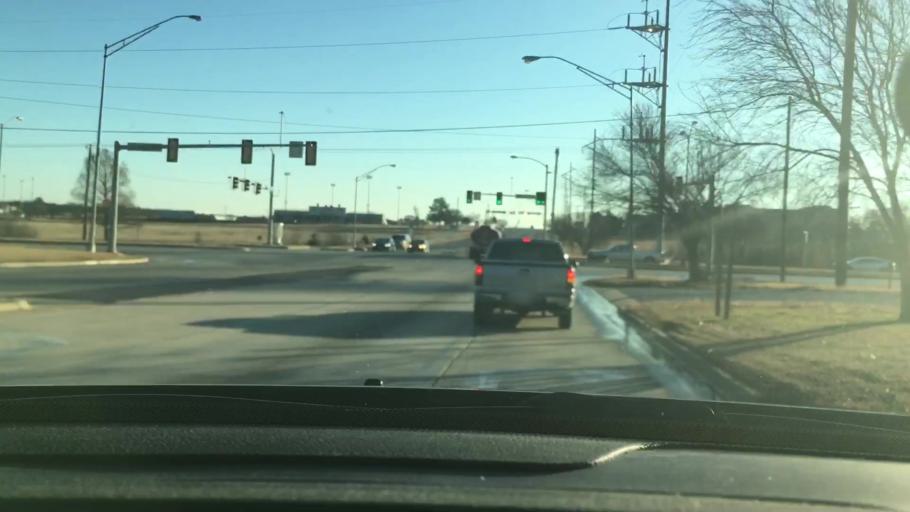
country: US
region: Oklahoma
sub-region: Carter County
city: Ardmore
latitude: 34.2028
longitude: -97.1439
